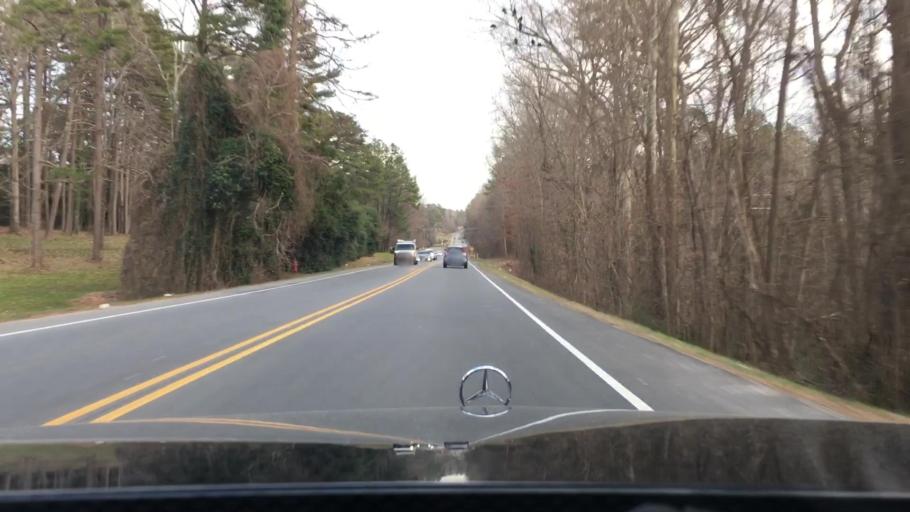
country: US
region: North Carolina
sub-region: Orange County
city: Hillsborough
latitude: 36.0859
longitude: -79.0974
